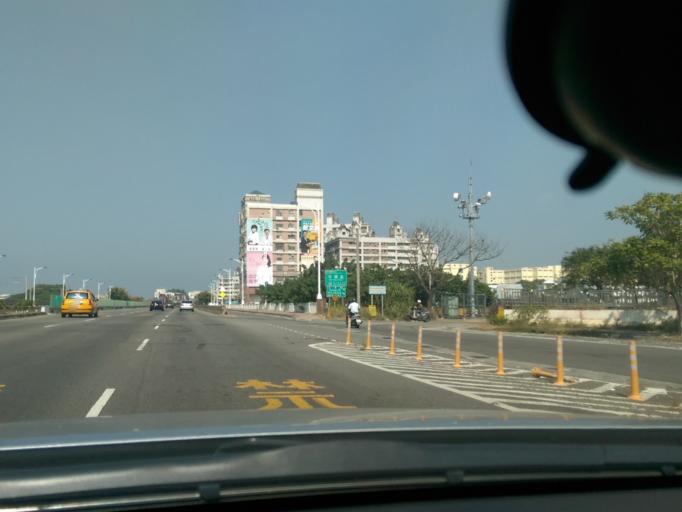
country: TW
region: Taiwan
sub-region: Chiayi
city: Jiayi Shi
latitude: 23.5125
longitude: 120.4442
